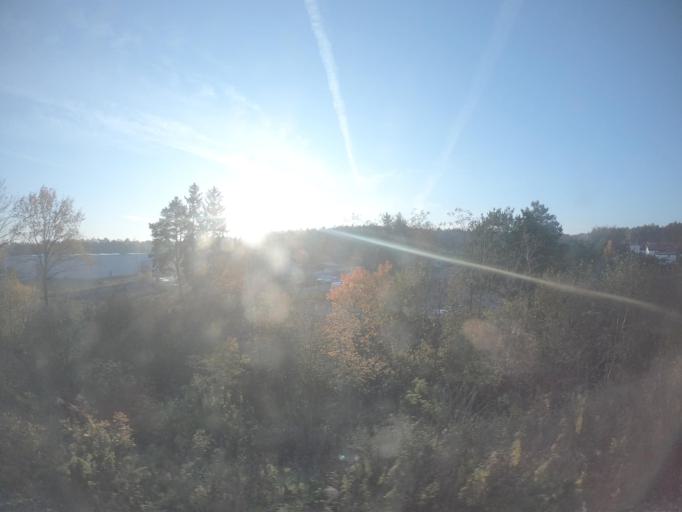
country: PL
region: Lubusz
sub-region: Powiat slubicki
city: Rzepin
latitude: 52.3391
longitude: 14.8305
